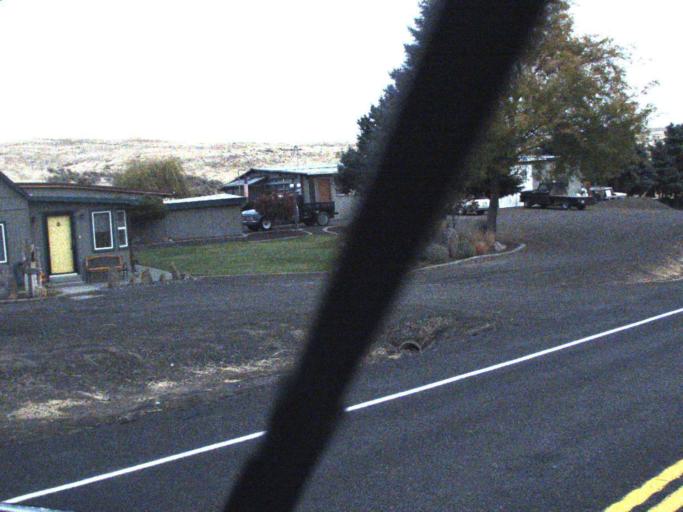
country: US
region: Washington
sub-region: Adams County
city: Ritzville
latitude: 46.7586
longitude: -118.3126
